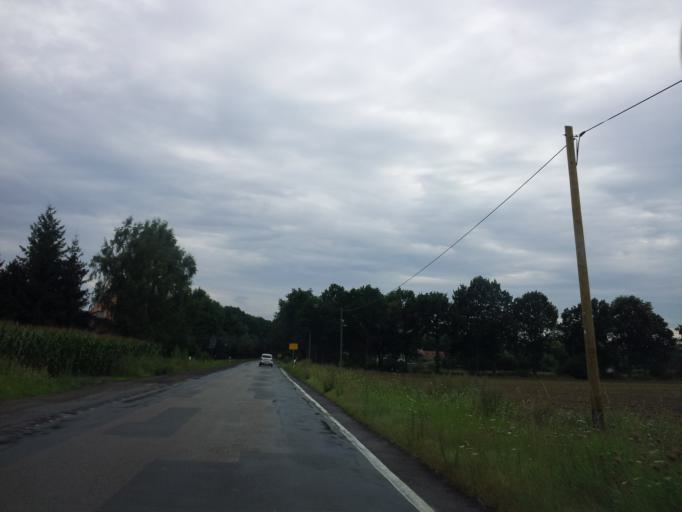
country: DE
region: Brandenburg
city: Gorzke
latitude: 52.1771
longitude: 12.3791
